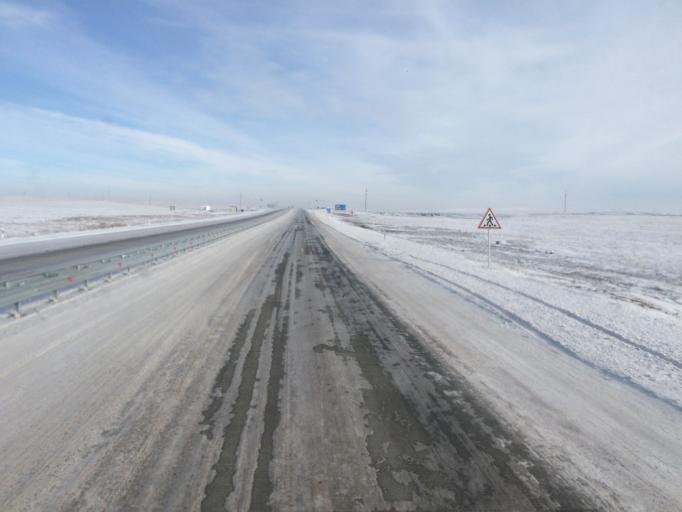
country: KZ
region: Zhambyl
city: Georgiyevka
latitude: 43.3510
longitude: 74.5502
